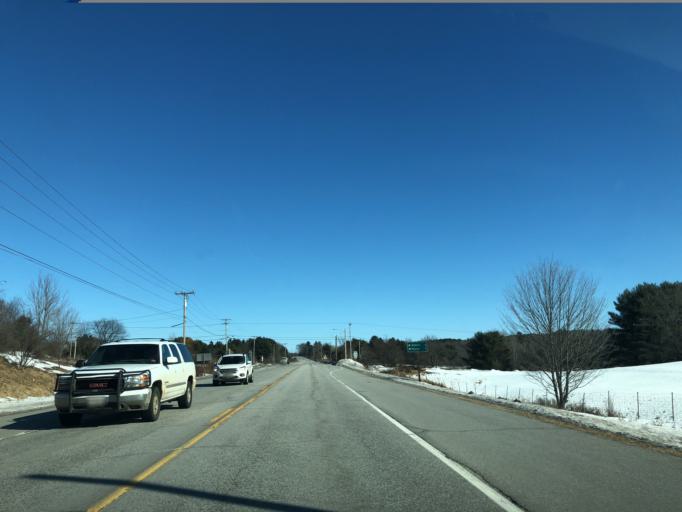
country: US
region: Maine
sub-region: Cumberland County
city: New Gloucester
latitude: 44.0228
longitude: -70.2784
